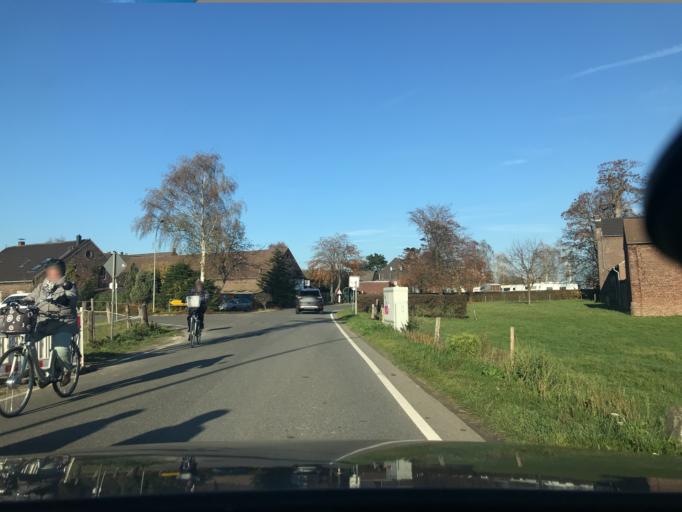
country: DE
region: North Rhine-Westphalia
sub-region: Regierungsbezirk Dusseldorf
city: Rheurdt
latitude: 51.4315
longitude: 6.4121
